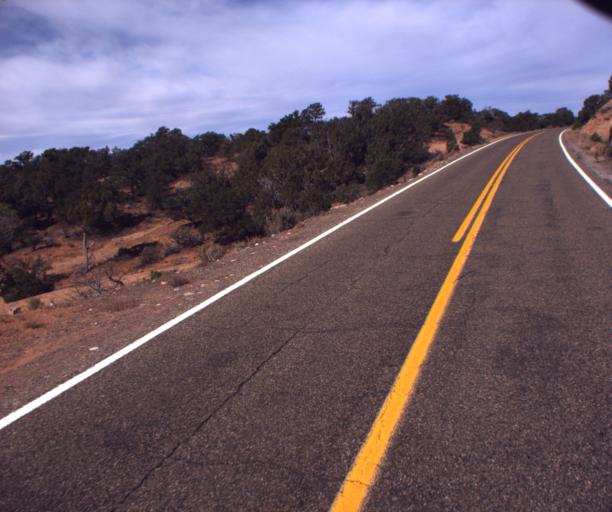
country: US
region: Arizona
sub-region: Navajo County
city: Kayenta
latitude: 36.6449
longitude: -110.5164
